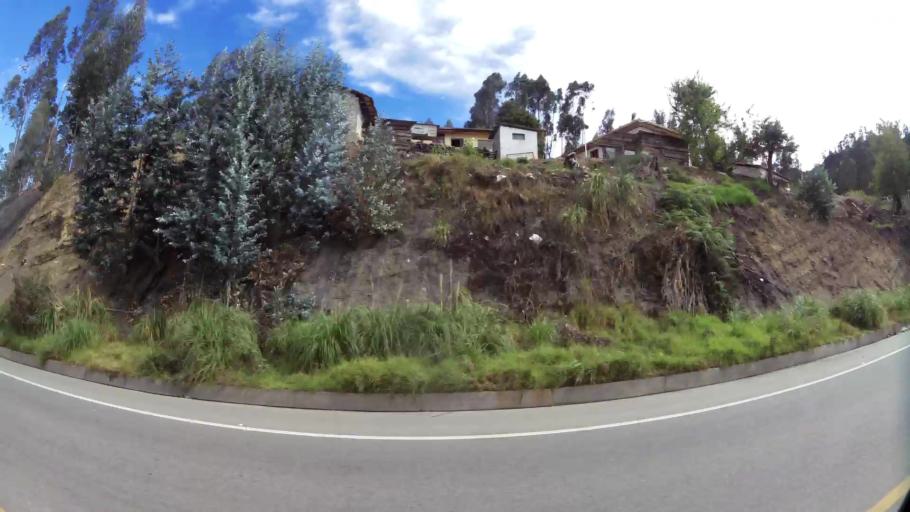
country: EC
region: Canar
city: Azogues
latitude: -2.7246
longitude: -78.8729
